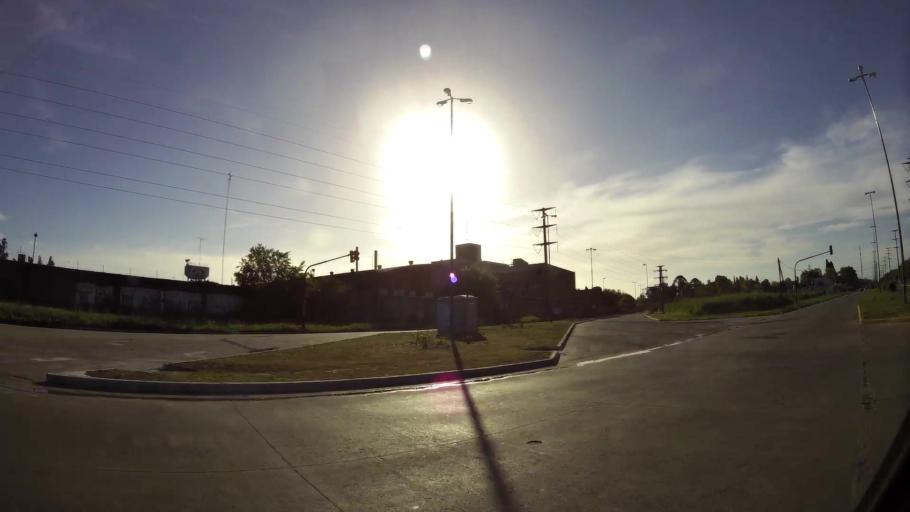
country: AR
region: Buenos Aires
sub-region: Partido de Quilmes
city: Quilmes
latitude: -34.8134
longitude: -58.2003
